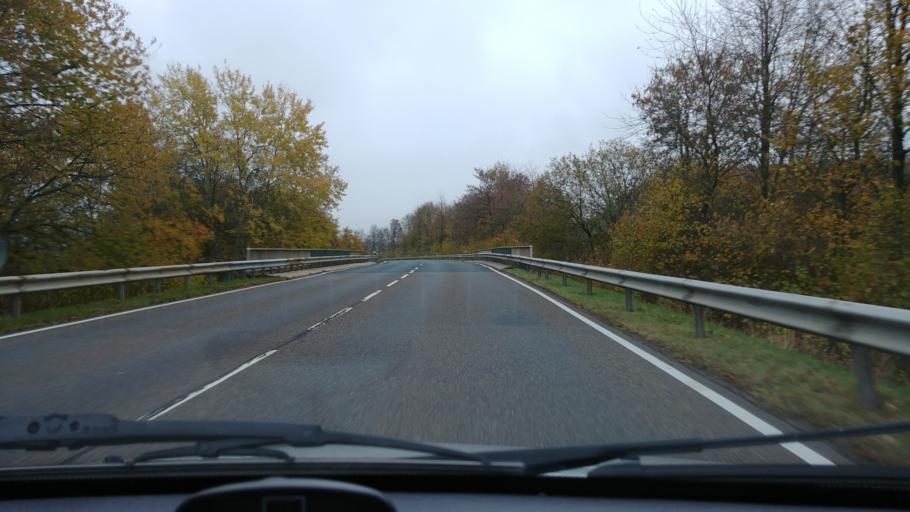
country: DE
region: Rheinland-Pfalz
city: Bellingen
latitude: 50.5987
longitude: 7.8932
